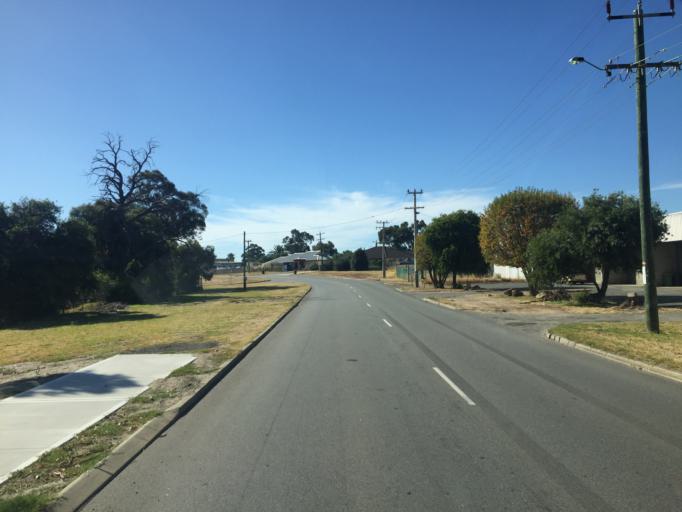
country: AU
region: Western Australia
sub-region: Gosnells
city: Maddington
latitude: -32.0408
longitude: 115.9841
